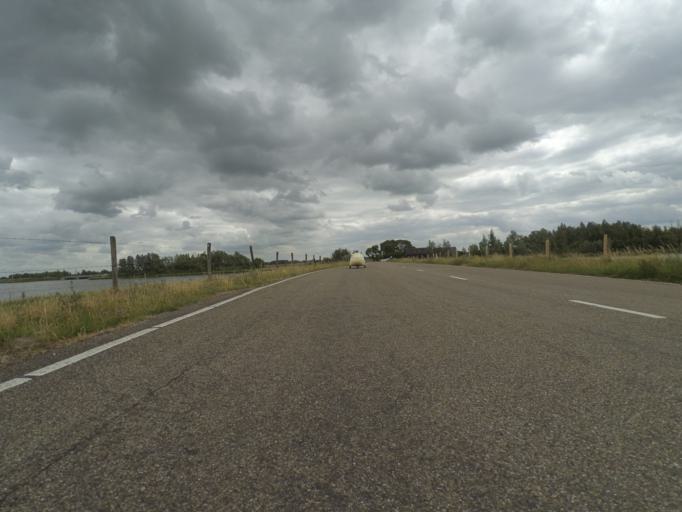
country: NL
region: South Holland
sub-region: Gemeente Sliedrecht
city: Sliedrecht
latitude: 51.7853
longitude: 4.7693
